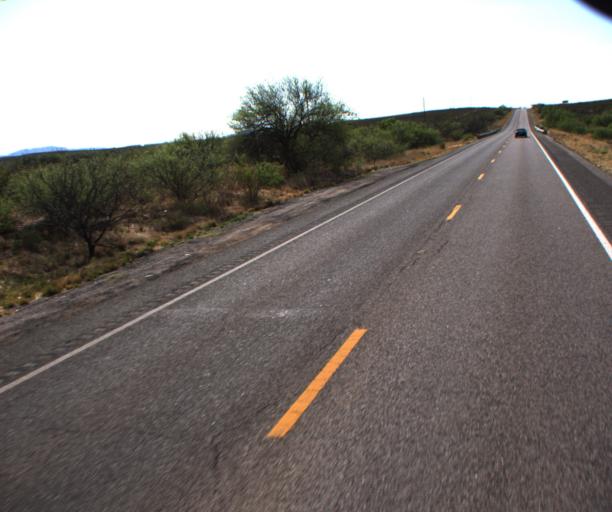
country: US
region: Arizona
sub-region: Cochise County
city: Tombstone
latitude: 31.7556
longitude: -110.1055
